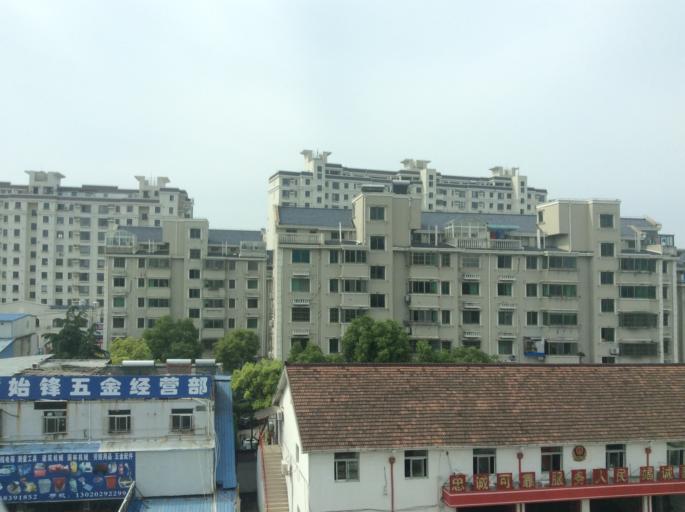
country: CN
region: Shanghai Shi
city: Kangqiao
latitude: 31.2019
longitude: 121.6939
